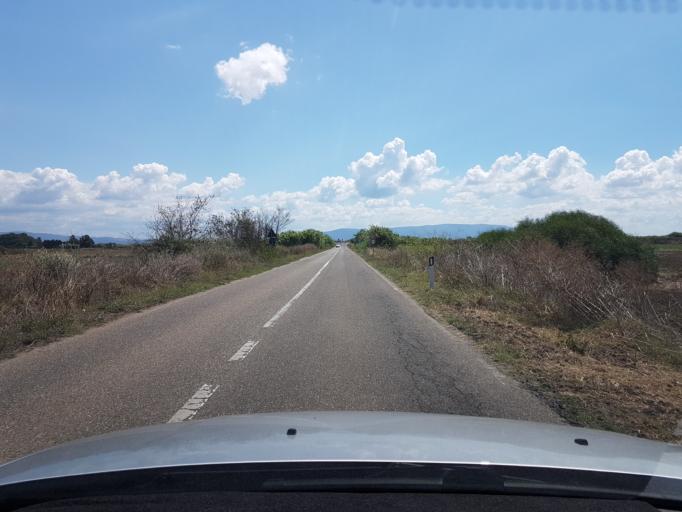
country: IT
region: Sardinia
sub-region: Provincia di Oristano
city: Solanas
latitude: 39.9195
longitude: 8.5499
